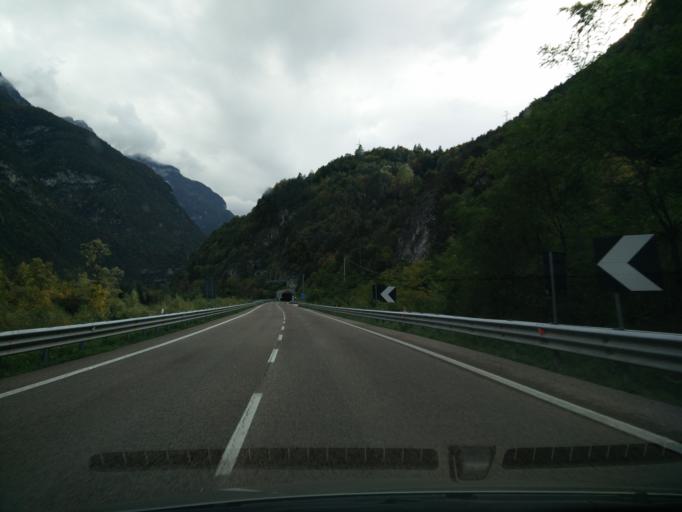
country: IT
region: Veneto
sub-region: Provincia di Belluno
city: Ospitale di Cadore
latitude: 46.3449
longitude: 12.3312
